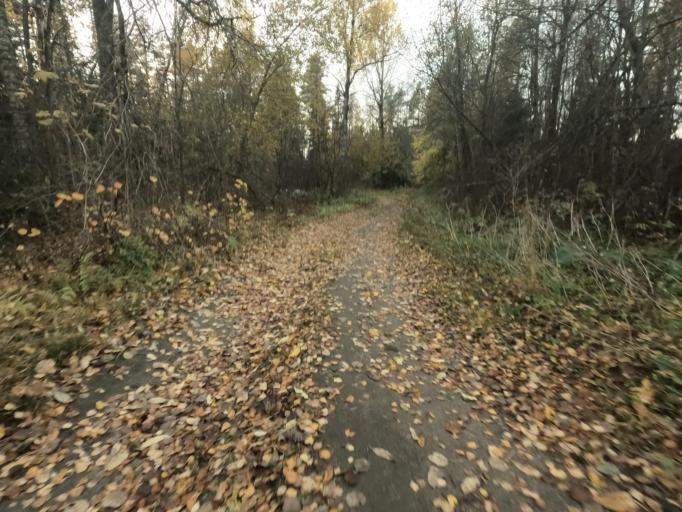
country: RU
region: Leningrad
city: Leninskoye
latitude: 60.1951
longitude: 29.8544
